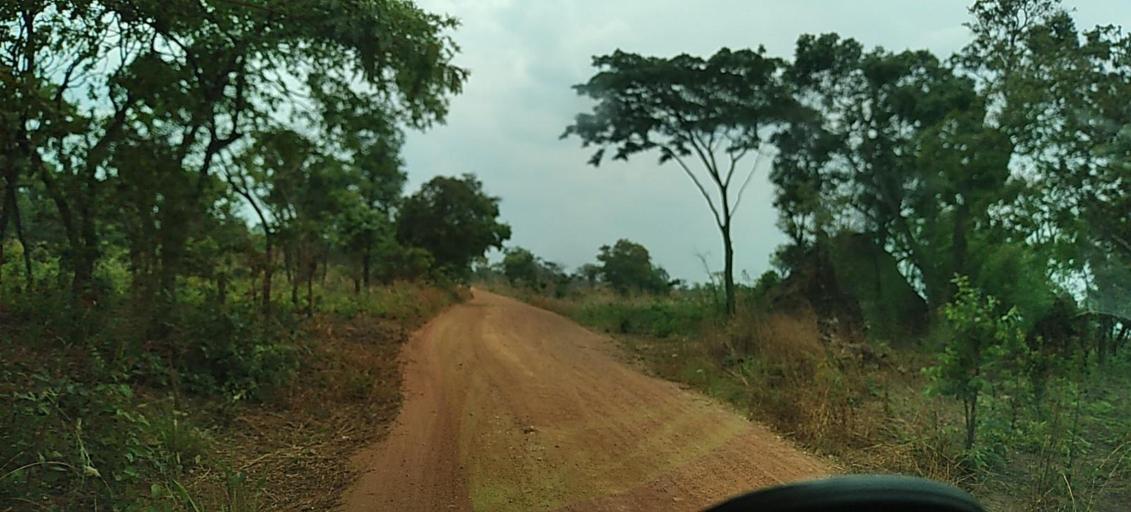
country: ZM
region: North-Western
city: Kansanshi
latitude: -12.0792
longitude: 26.3588
